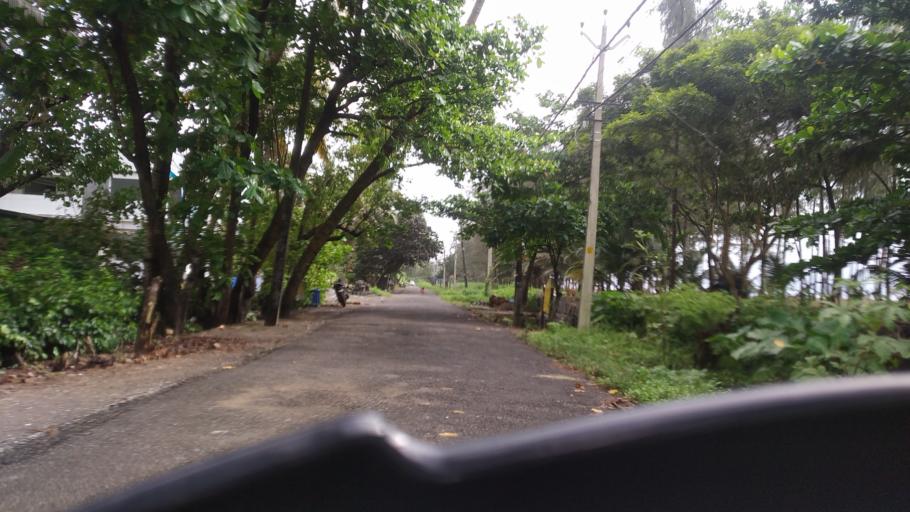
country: IN
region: Kerala
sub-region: Thrissur District
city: Kodungallur
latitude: 10.1257
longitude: 76.1835
